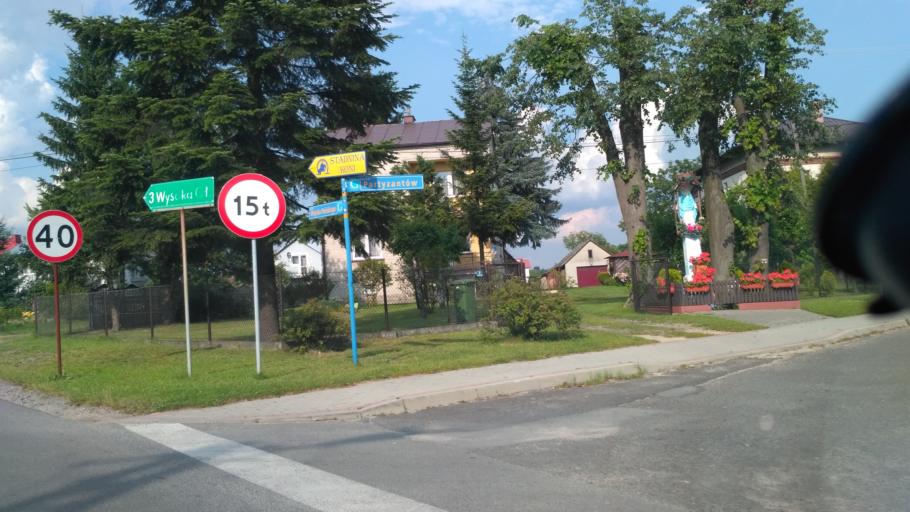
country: PL
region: Subcarpathian Voivodeship
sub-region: Powiat rzeszowski
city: Glogow Malopolski
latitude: 50.1519
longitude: 21.9689
